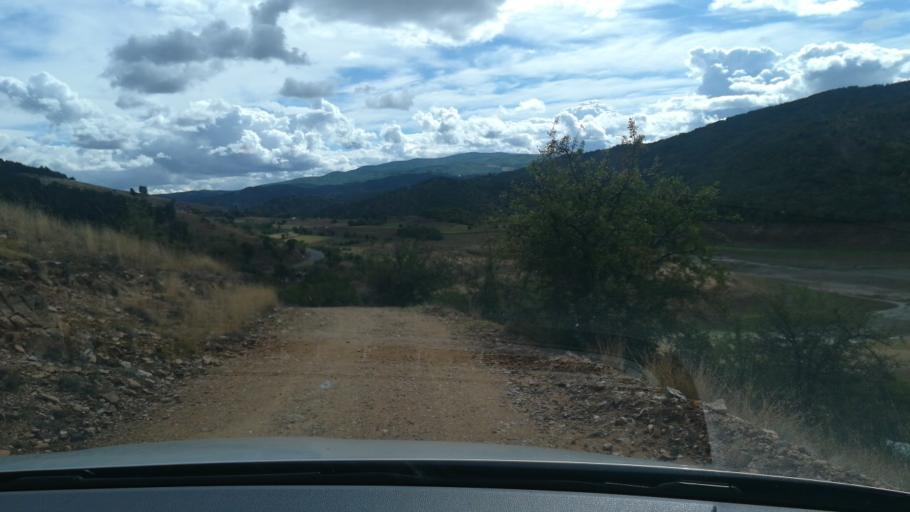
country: MK
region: Makedonska Kamenica
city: Makedonska Kamenica
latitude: 42.0039
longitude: 22.6088
